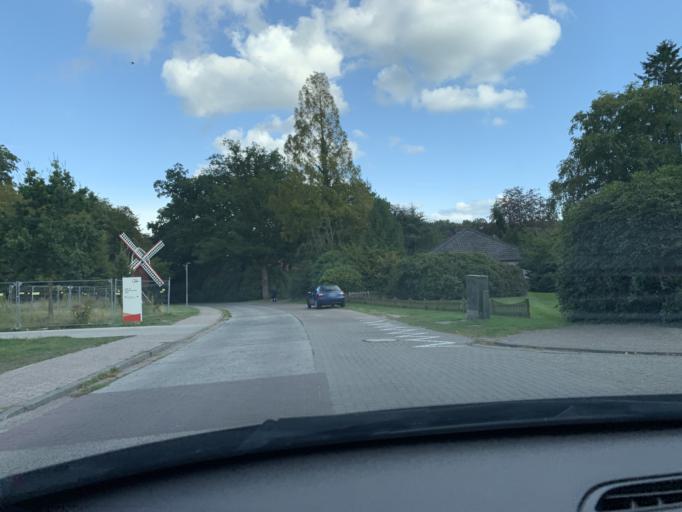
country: DE
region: Lower Saxony
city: Bad Zwischenahn
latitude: 53.1923
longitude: 7.9875
